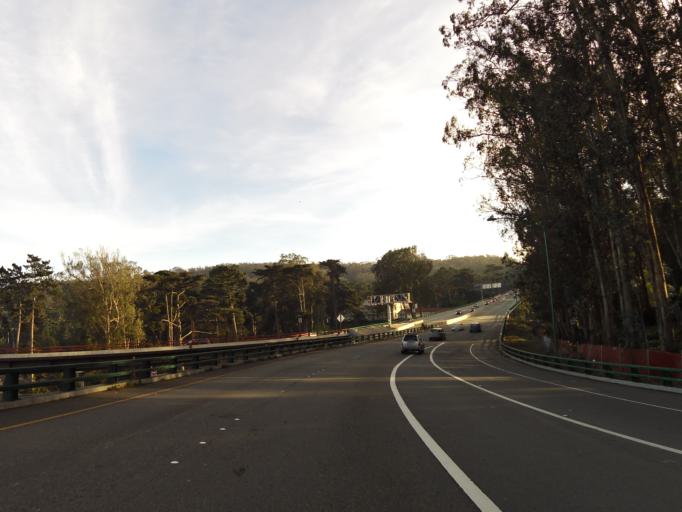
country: US
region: California
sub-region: San Francisco County
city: San Francisco
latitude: 37.8026
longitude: -122.4697
